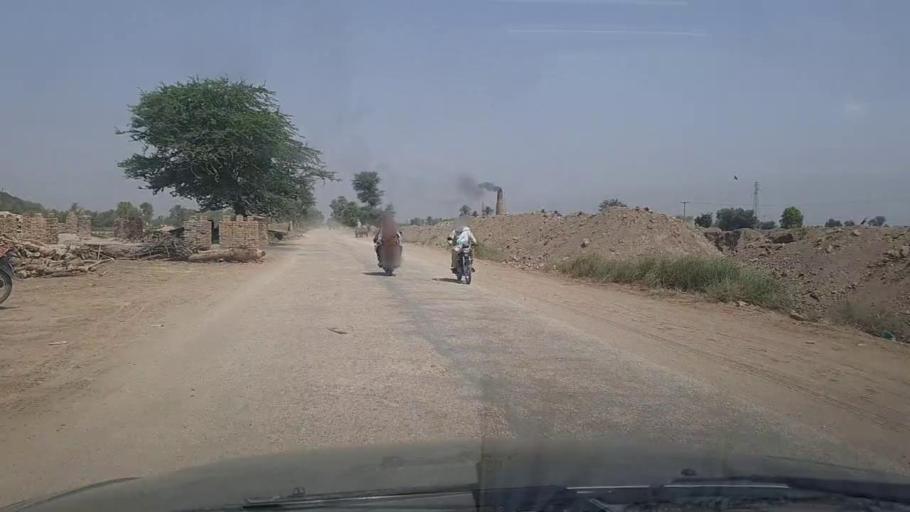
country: PK
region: Sindh
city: Setharja Old
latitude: 27.1476
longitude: 68.5246
